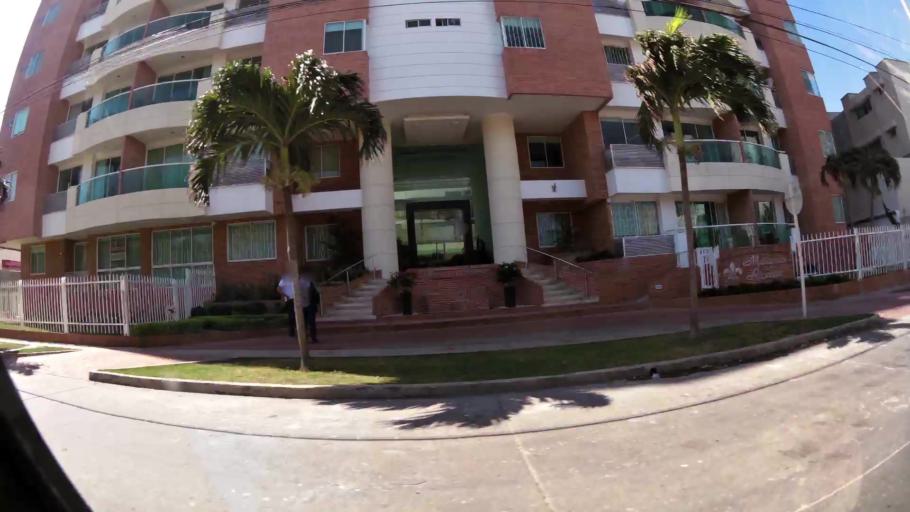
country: CO
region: Atlantico
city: Barranquilla
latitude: 11.0148
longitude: -74.8176
